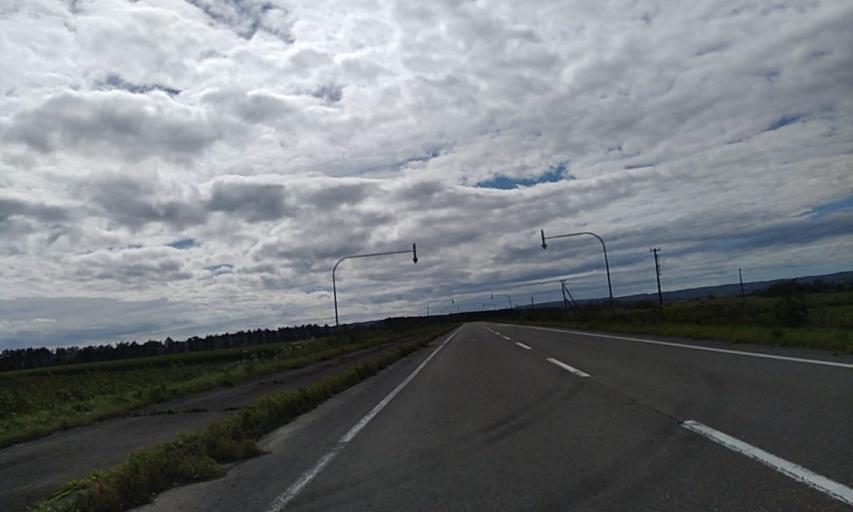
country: JP
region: Hokkaido
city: Obihiro
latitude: 42.7185
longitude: 143.6463
